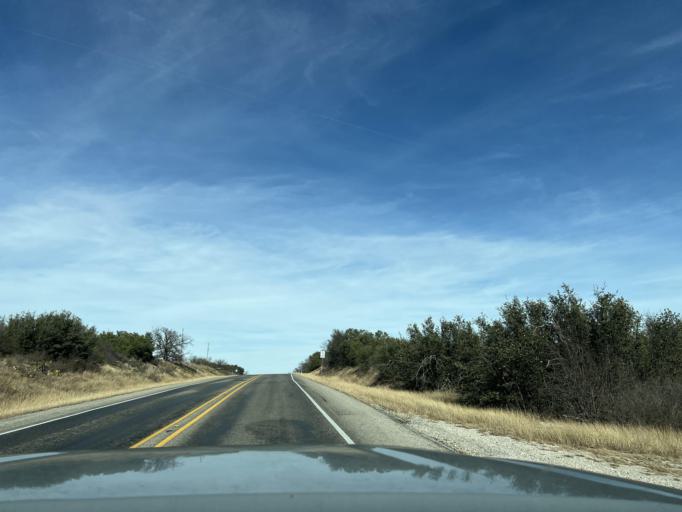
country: US
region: Texas
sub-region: Eastland County
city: Cisco
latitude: 32.4271
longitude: -98.9863
